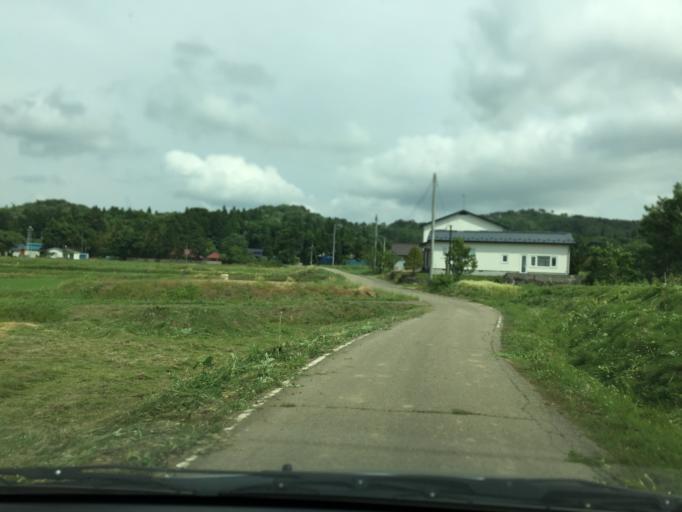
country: JP
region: Fukushima
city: Inawashiro
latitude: 37.5359
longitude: 139.9699
